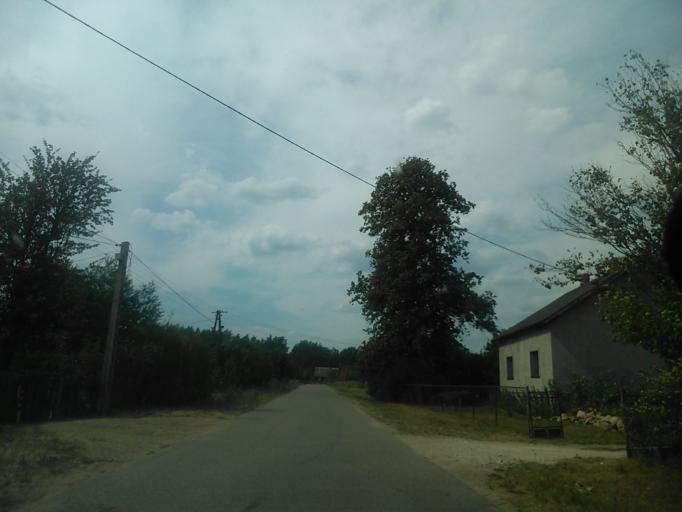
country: PL
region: Masovian Voivodeship
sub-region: Powiat ostrolecki
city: Czarnia
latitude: 53.3822
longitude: 21.1955
